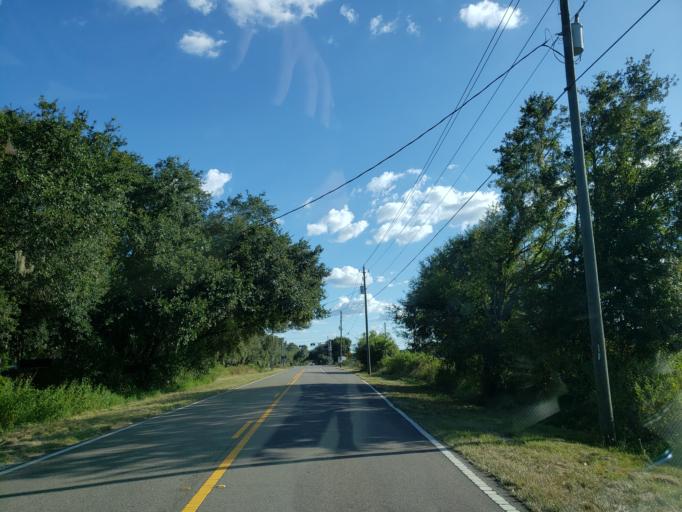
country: US
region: Florida
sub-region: Hillsborough County
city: Valrico
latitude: 27.9585
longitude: -82.2196
